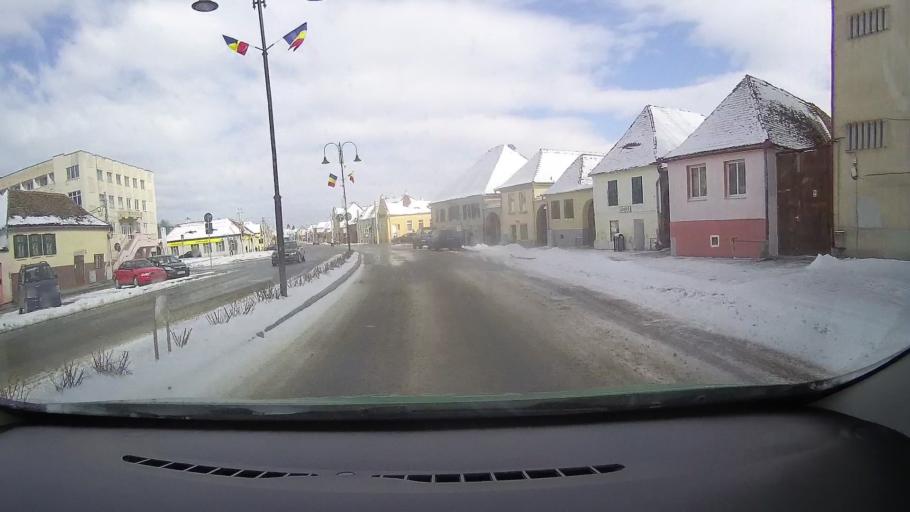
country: RO
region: Sibiu
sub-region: Oras Agnita
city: Agnita
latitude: 45.9755
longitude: 24.6264
